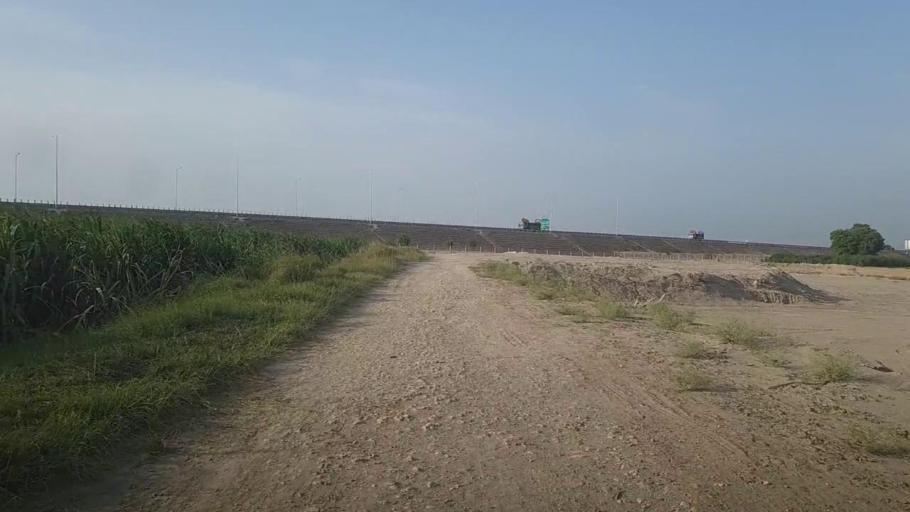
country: PK
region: Sindh
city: Ubauro
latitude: 28.3321
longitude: 69.7985
